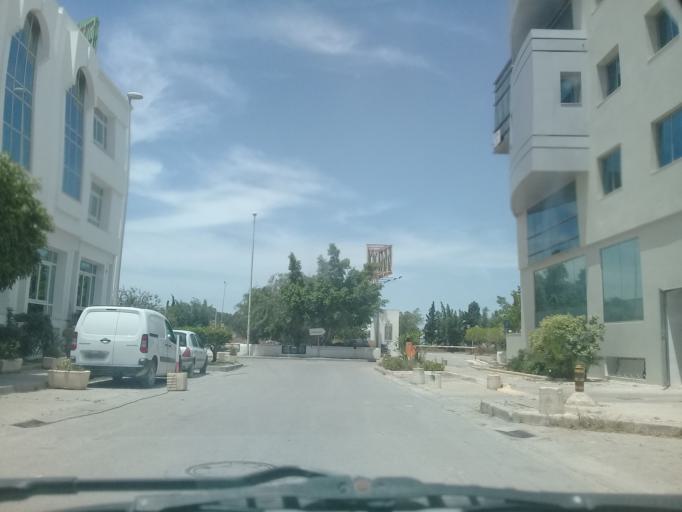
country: TN
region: Ariana
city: Ariana
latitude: 36.8358
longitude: 10.2295
